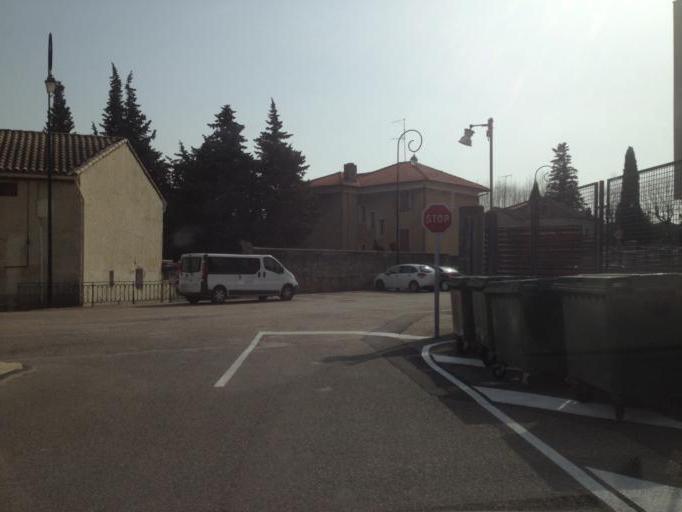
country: FR
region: Provence-Alpes-Cote d'Azur
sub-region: Departement du Vaucluse
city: Courthezon
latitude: 44.0903
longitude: 4.8853
